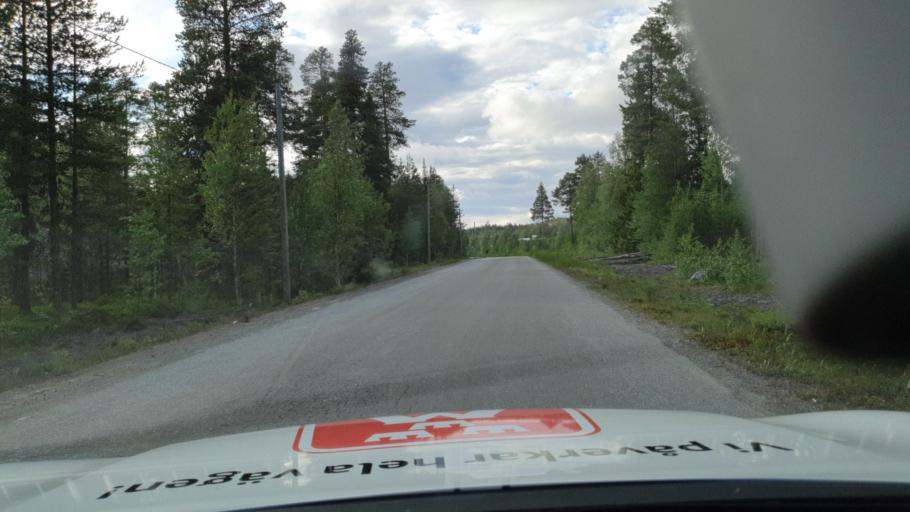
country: SE
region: Vaesterbotten
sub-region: Storumans Kommun
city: Storuman
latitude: 65.0705
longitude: 17.1252
